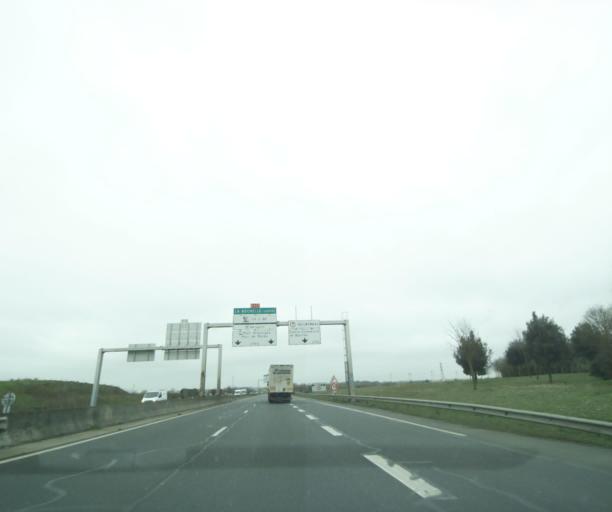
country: FR
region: Poitou-Charentes
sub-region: Departement de la Charente-Maritime
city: Puilboreau
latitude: 46.1753
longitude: -1.1245
